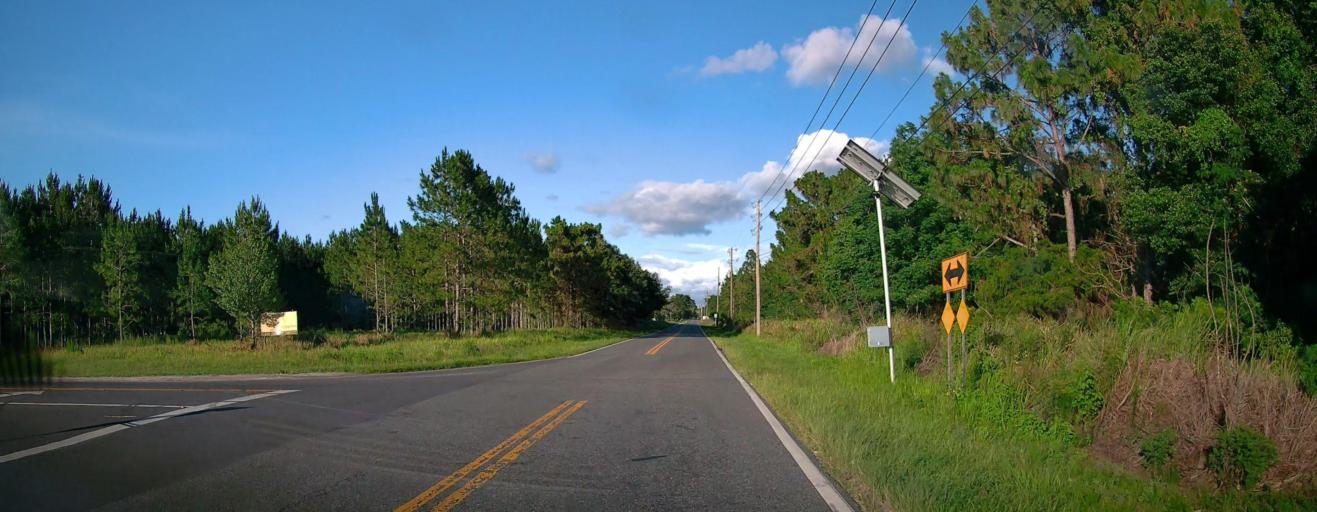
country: US
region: Florida
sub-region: Marion County
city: Silver Springs Shores
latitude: 29.0662
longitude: -82.0079
